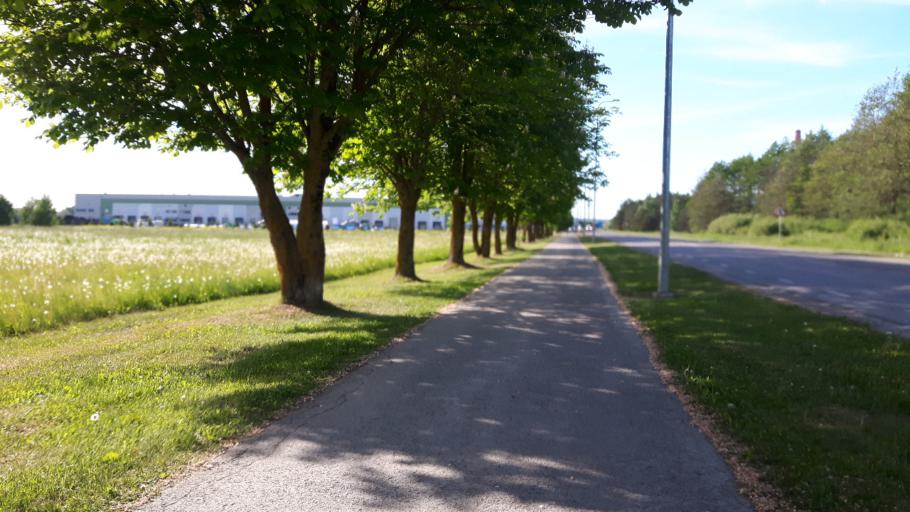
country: EE
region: Harju
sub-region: Joelaehtme vald
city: Loo
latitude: 59.4387
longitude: 24.9375
